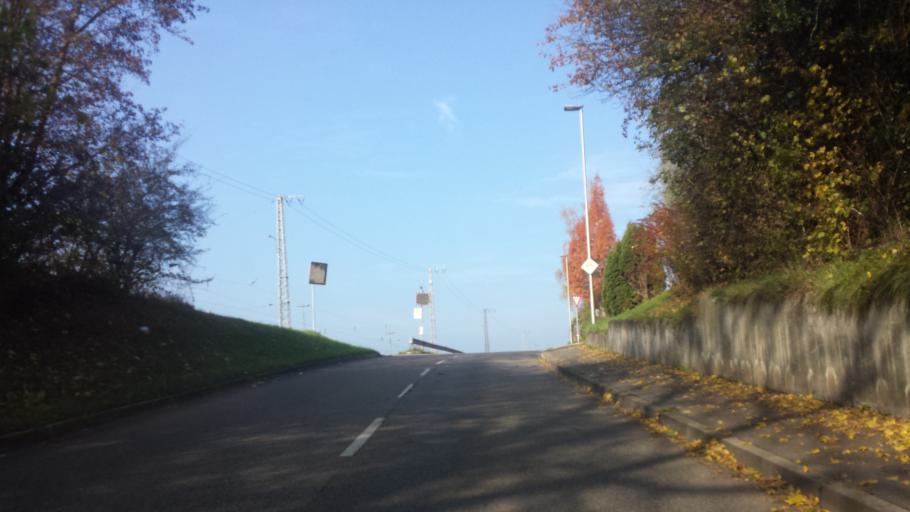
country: DE
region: Baden-Wuerttemberg
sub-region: Karlsruhe Region
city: Obrigheim
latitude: 49.3460
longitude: 9.1159
